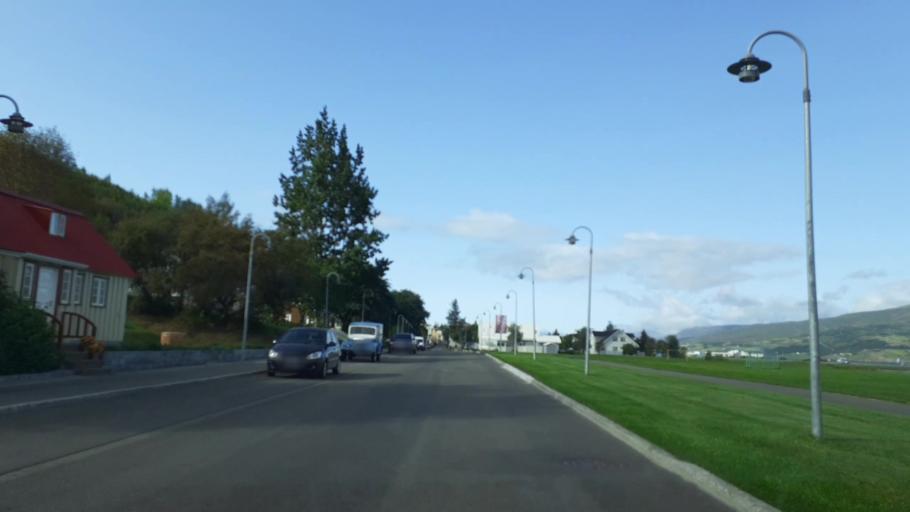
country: IS
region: Northeast
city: Akureyri
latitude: 65.6674
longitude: -18.0852
